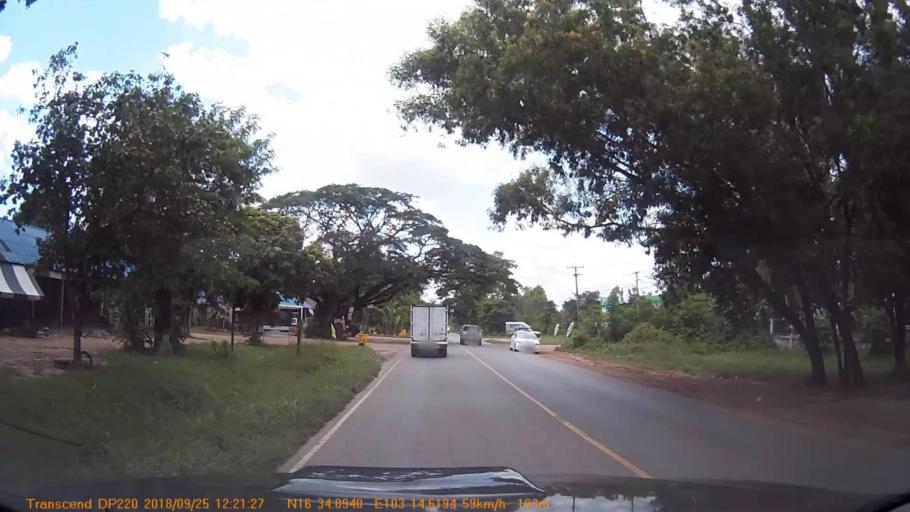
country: TH
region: Kalasin
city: Huai Mek
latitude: 16.5815
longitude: 103.2437
